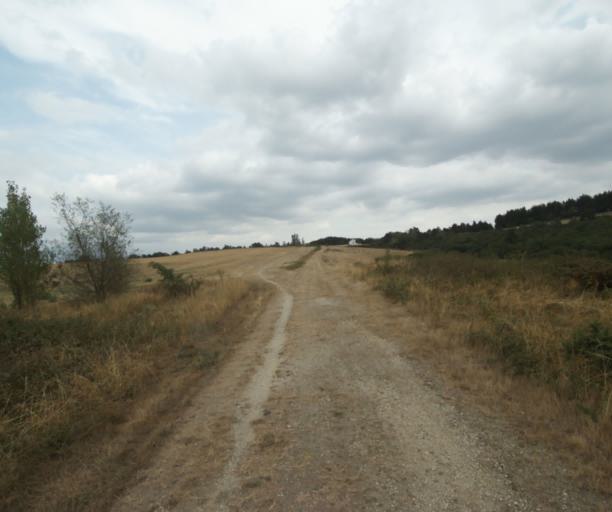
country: FR
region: Midi-Pyrenees
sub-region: Departement de la Haute-Garonne
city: Revel
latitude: 43.4439
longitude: 2.0112
